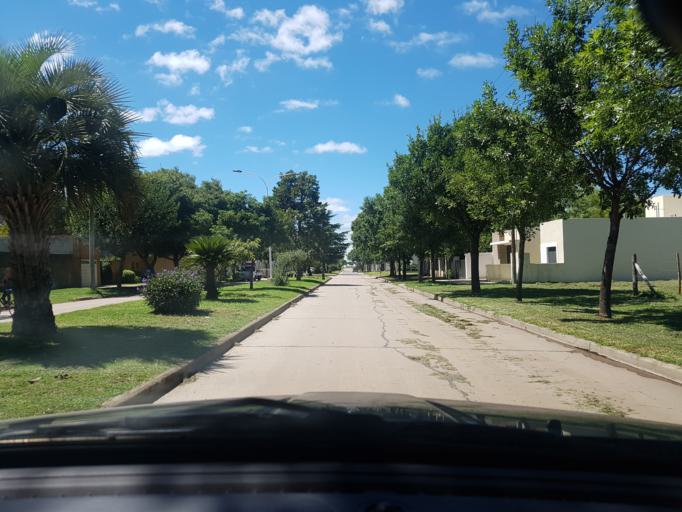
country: AR
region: Cordoba
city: General Cabrera
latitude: -32.7603
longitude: -63.7912
